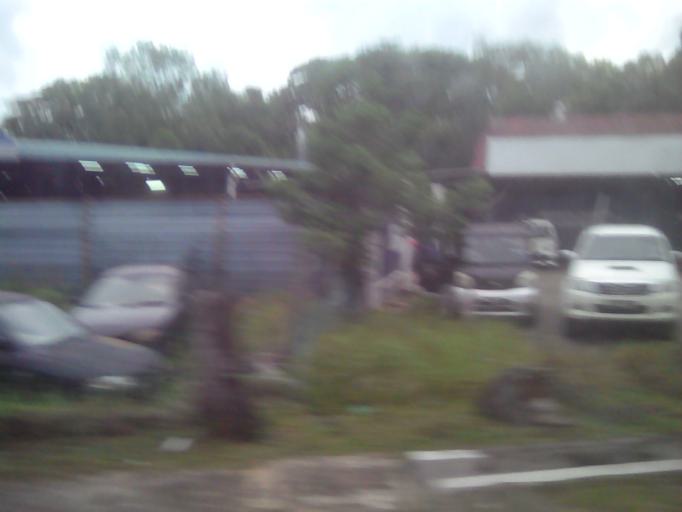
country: MY
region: Penang
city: Butterworth
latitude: 5.3973
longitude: 100.3686
